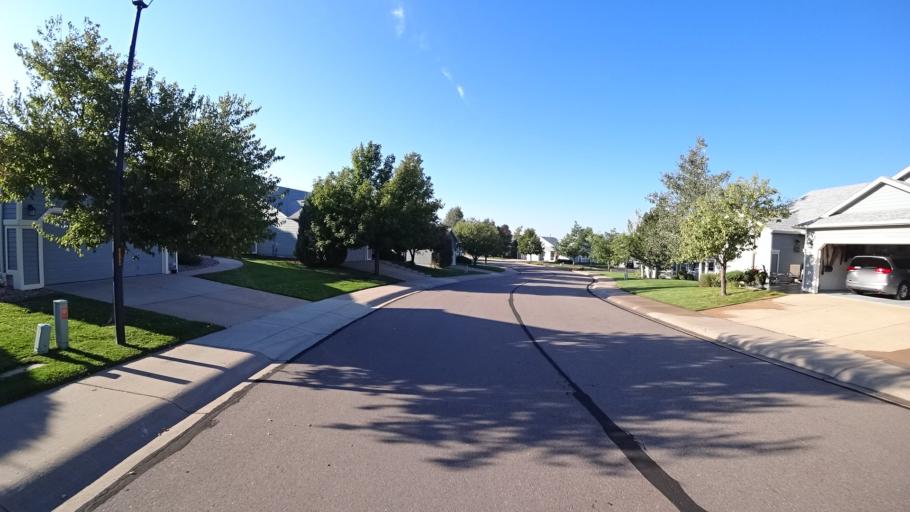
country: US
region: Colorado
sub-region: El Paso County
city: Cimarron Hills
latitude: 38.8907
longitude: -104.7070
